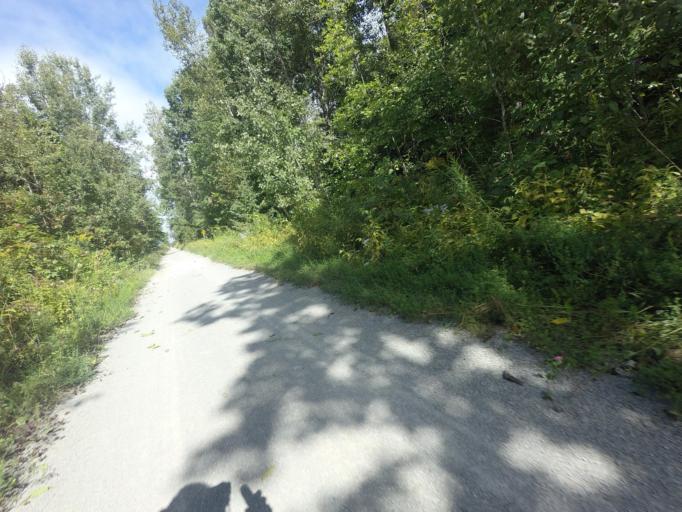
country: CA
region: Ontario
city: Uxbridge
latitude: 44.1844
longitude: -79.0689
